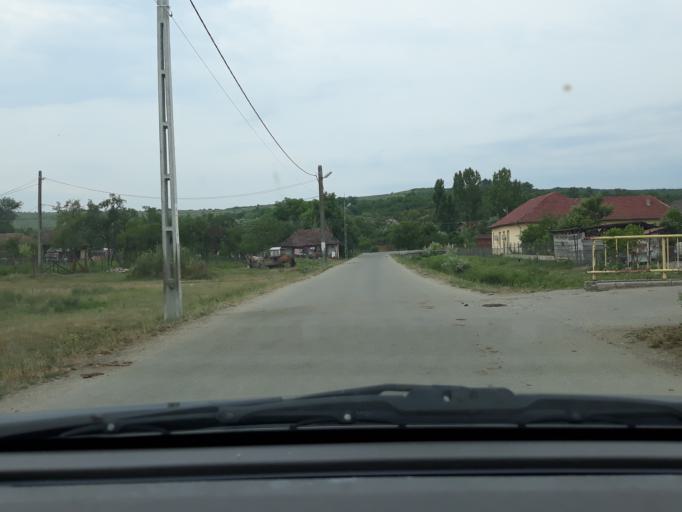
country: RO
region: Salaj
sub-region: Comuna Criseni
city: Criseni
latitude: 47.2582
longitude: 23.0632
